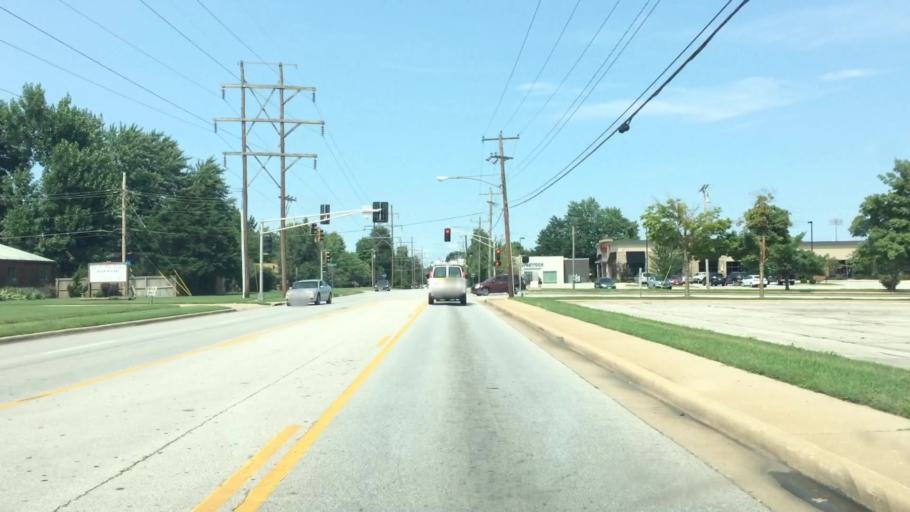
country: US
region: Missouri
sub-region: Greene County
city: Springfield
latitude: 37.1620
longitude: -93.2717
